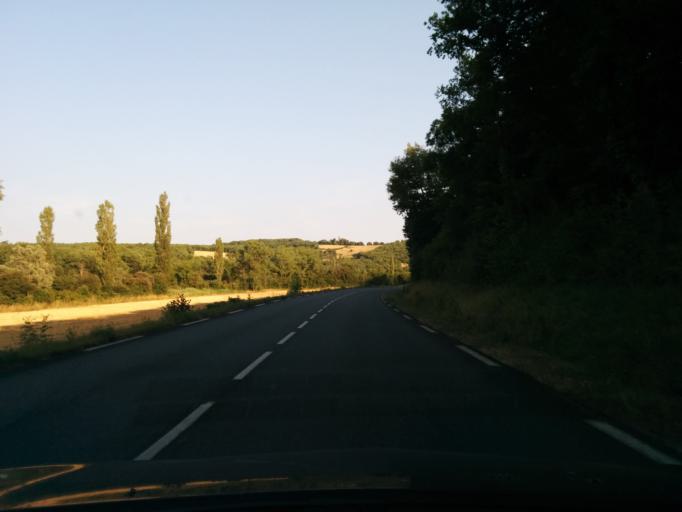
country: FR
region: Midi-Pyrenees
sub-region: Departement du Lot
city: Le Vigan
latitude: 44.6948
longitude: 1.4827
